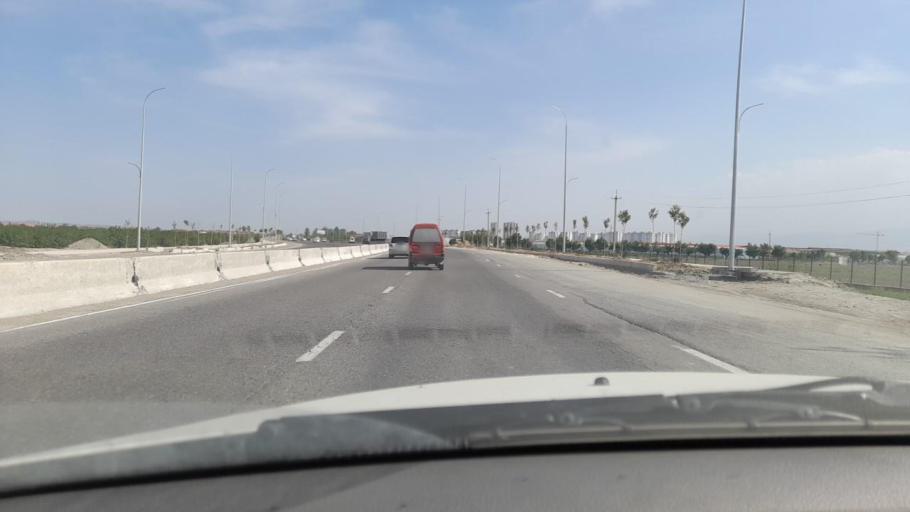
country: UZ
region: Samarqand
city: Daxbet
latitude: 39.7406
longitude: 66.9271
